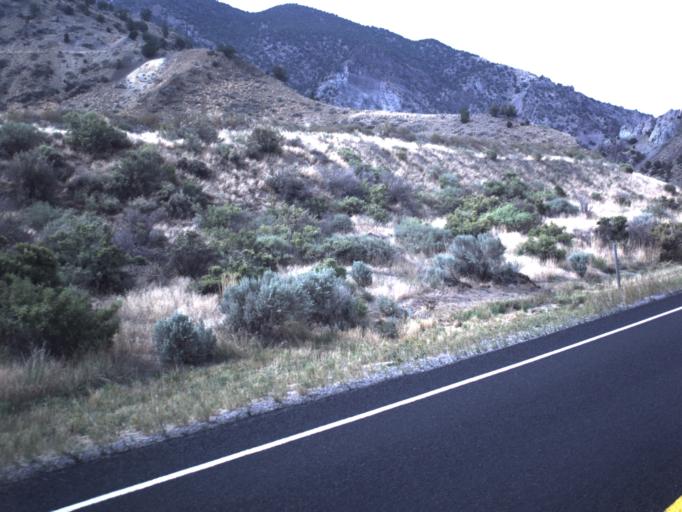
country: US
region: Utah
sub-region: Sevier County
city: Monroe
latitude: 38.5226
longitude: -112.2654
